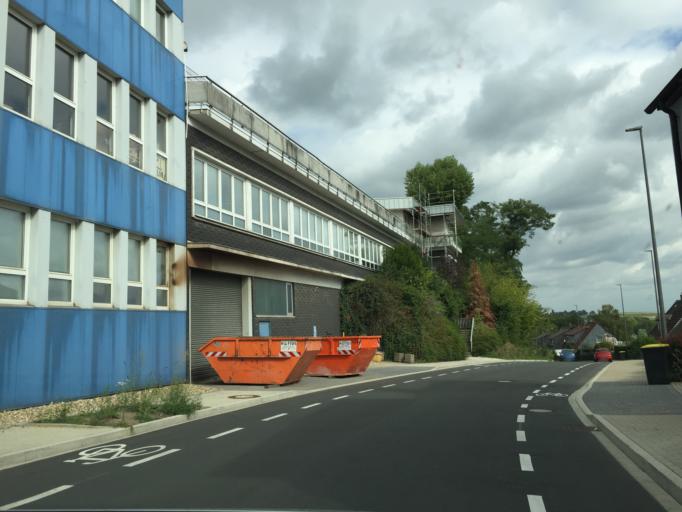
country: DE
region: North Rhine-Westphalia
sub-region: Regierungsbezirk Dusseldorf
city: Heiligenhaus
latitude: 51.3270
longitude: 6.9543
